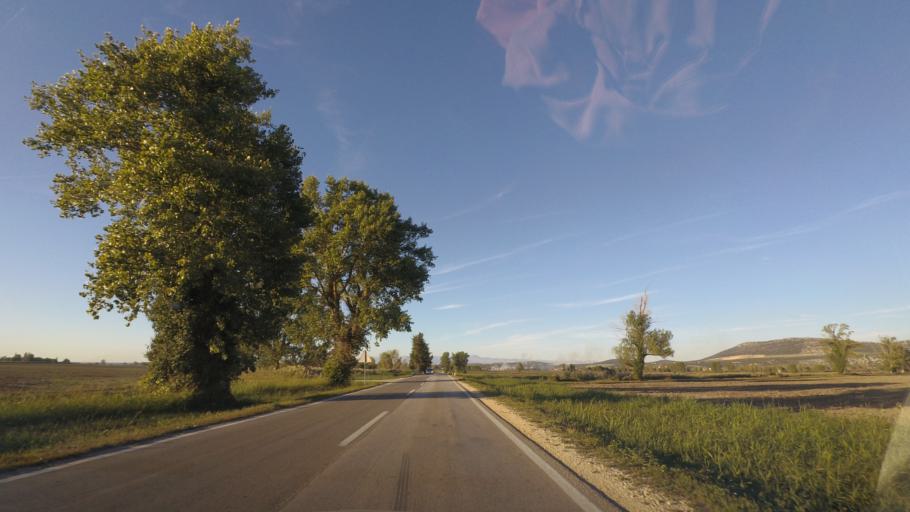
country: HR
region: Zadarska
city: Biograd na Moru
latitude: 43.9668
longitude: 15.4839
